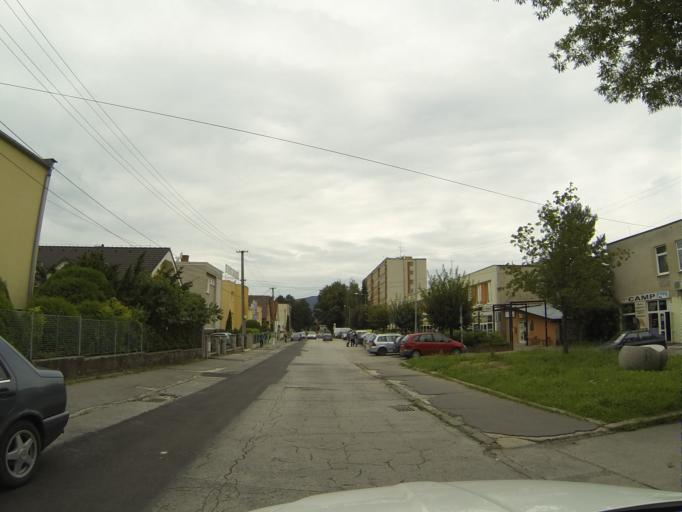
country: SK
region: Nitriansky
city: Prievidza
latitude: 48.7759
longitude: 18.6248
